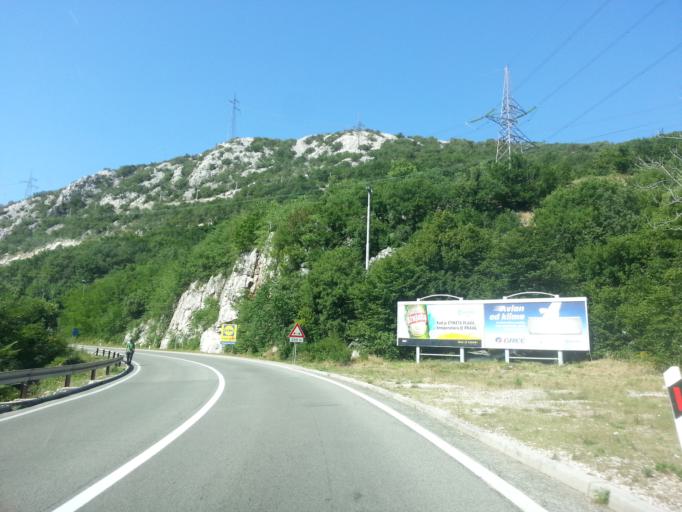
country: HR
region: Primorsko-Goranska
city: Bakar
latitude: 45.3094
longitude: 14.5279
